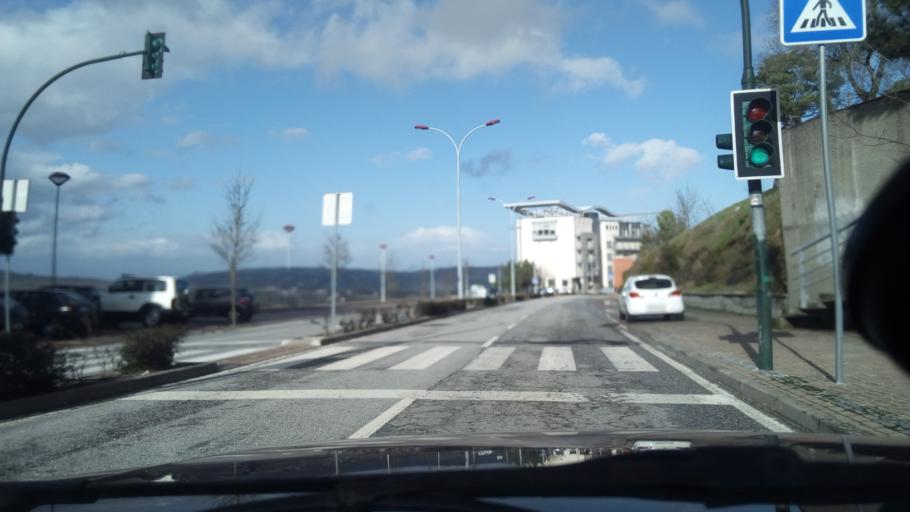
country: PT
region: Guarda
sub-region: Guarda
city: Guarda
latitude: 40.5419
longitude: -7.2683
